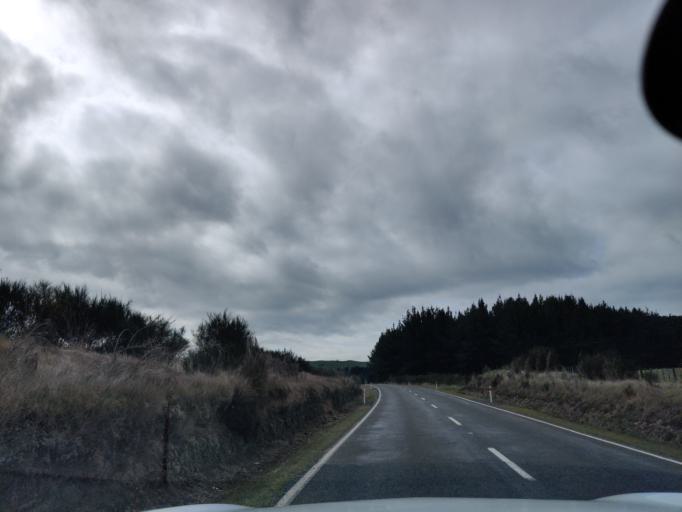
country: NZ
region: Waikato
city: Turangi
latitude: -38.8386
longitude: 175.6885
